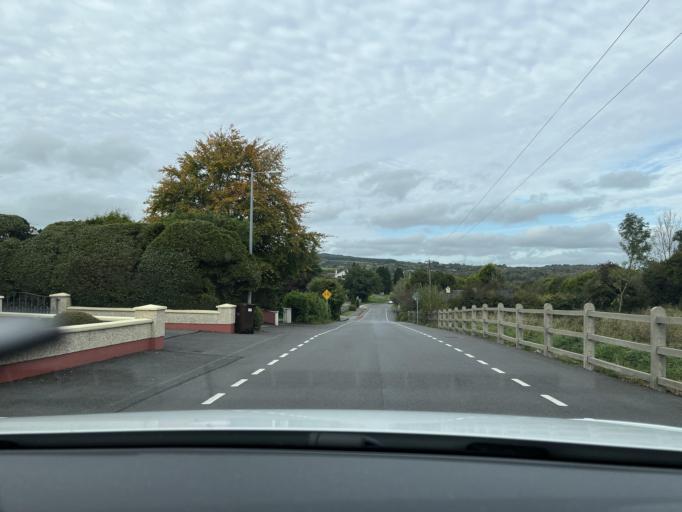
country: IE
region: Connaught
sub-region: Roscommon
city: Boyle
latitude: 53.9789
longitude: -8.2771
